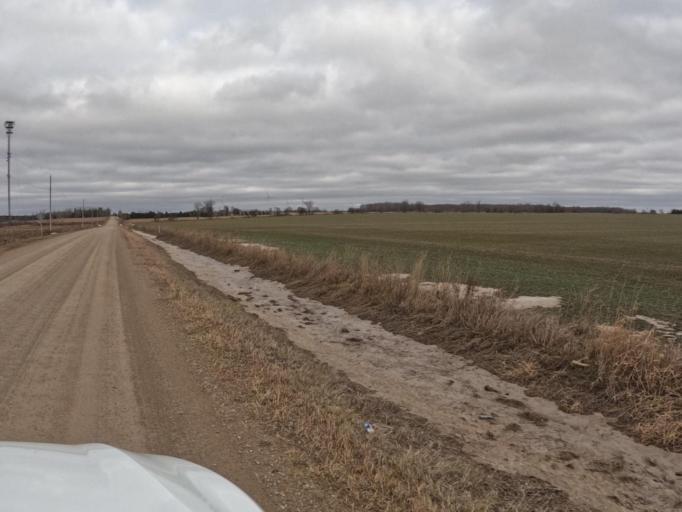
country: CA
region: Ontario
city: Shelburne
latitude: 43.8631
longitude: -80.3770
